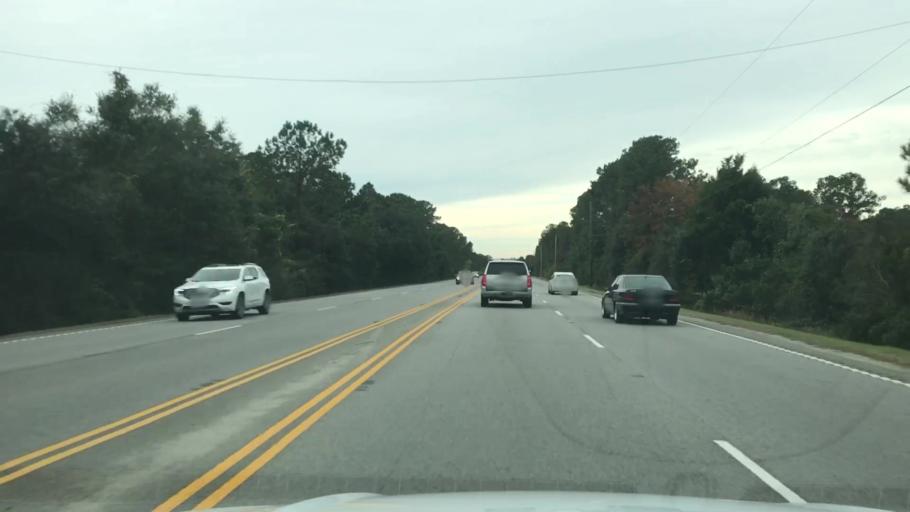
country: US
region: South Carolina
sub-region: Georgetown County
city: Georgetown
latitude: 33.3646
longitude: -79.2407
